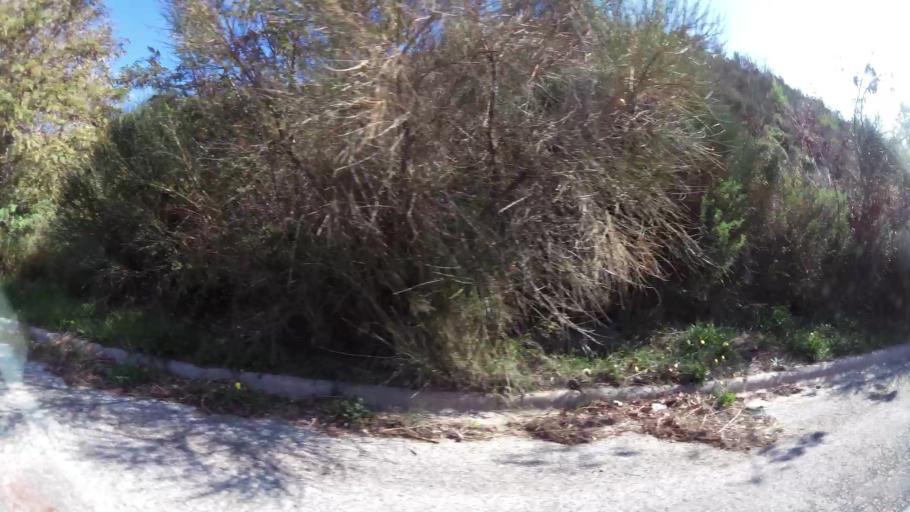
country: GR
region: Attica
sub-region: Nomarchia Anatolikis Attikis
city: Dhrafi
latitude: 38.0456
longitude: 23.8948
